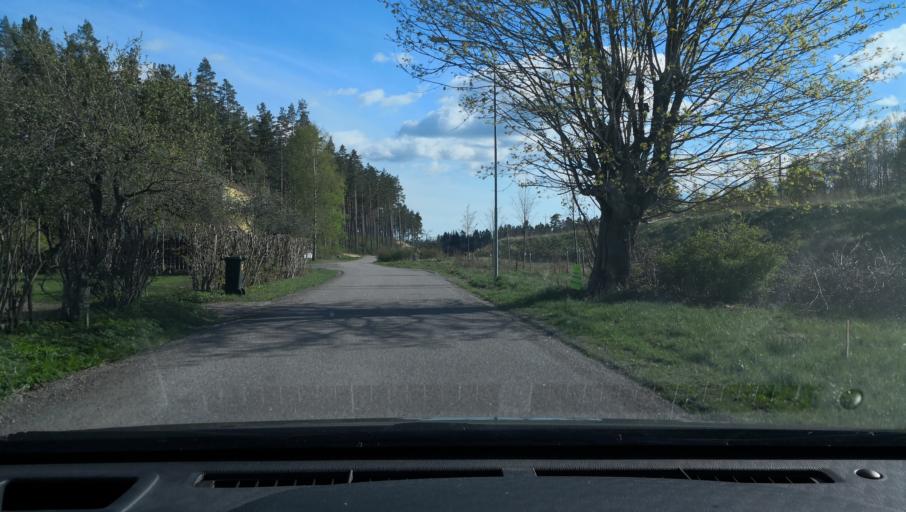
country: SE
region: OErebro
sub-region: Askersunds Kommun
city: Asbro
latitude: 58.9476
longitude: 15.0417
